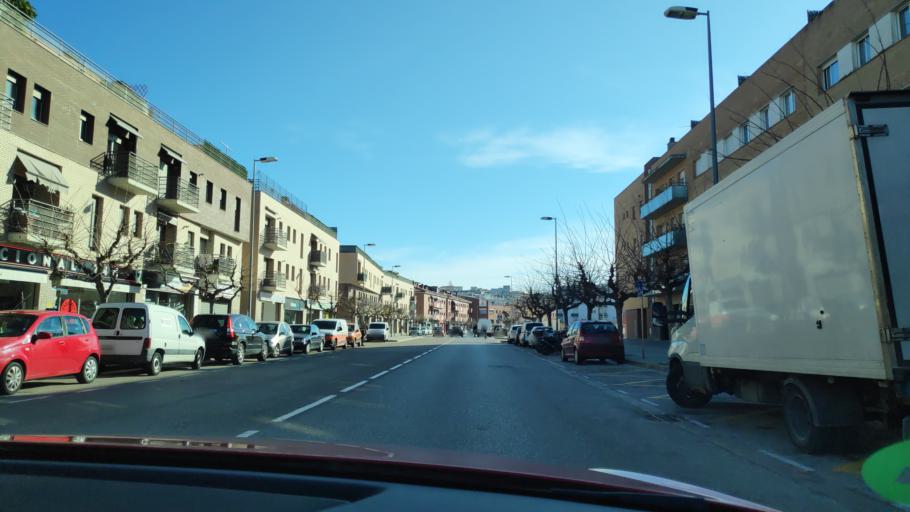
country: ES
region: Catalonia
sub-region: Provincia de Girona
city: Lloret de Mar
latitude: 41.7100
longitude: 2.8391
